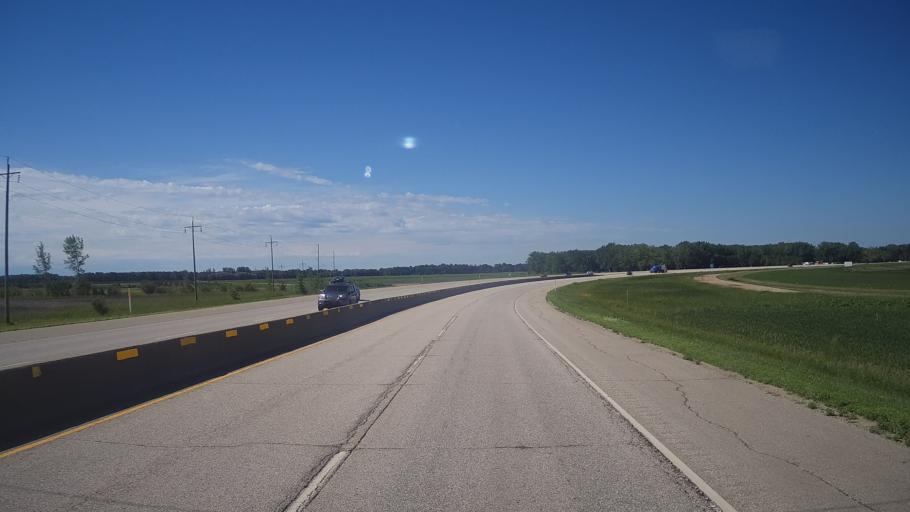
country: CA
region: Manitoba
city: Portage la Prairie
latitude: 49.9644
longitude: -98.2371
